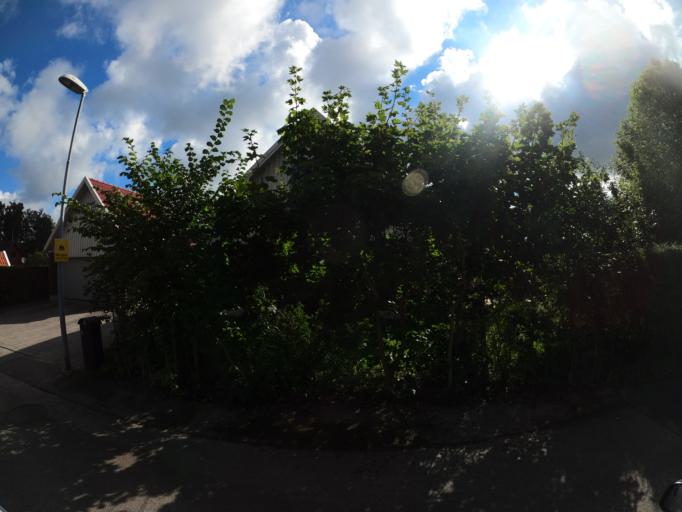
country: SE
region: Skane
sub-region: Lunds Kommun
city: Genarp
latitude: 55.5998
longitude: 13.3924
